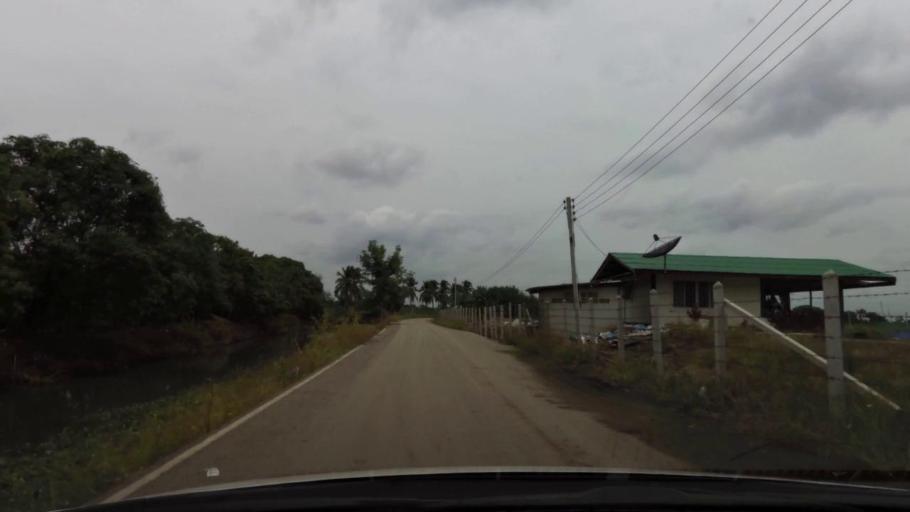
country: TH
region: Samut Sakhon
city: Ban Phaeo
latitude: 13.6124
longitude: 100.0315
